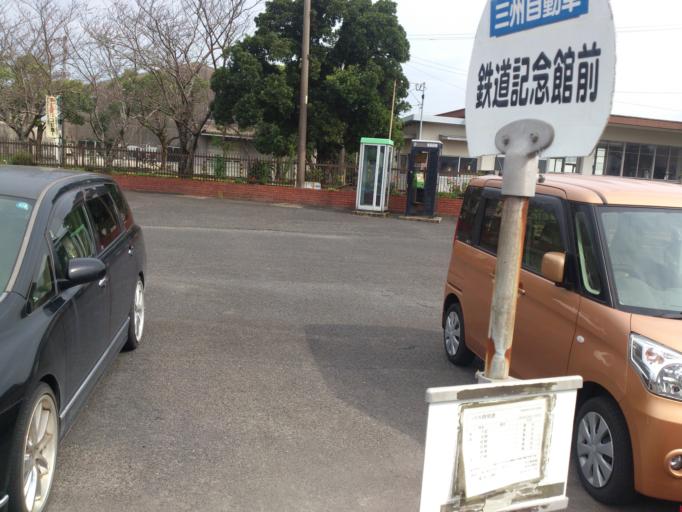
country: JP
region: Kagoshima
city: Kanoya
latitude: 31.3502
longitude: 130.9406
